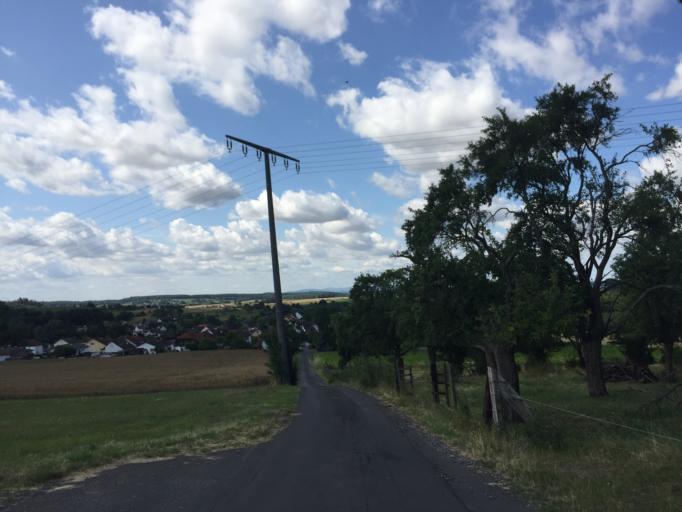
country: DE
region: Hesse
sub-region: Regierungsbezirk Giessen
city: Grunberg
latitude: 50.5757
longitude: 8.9727
